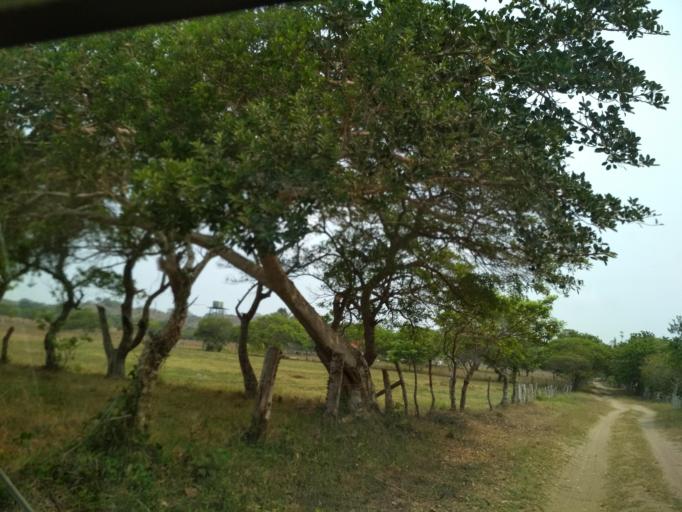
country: MX
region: Veracruz
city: Anton Lizardo
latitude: 19.0147
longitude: -95.9887
